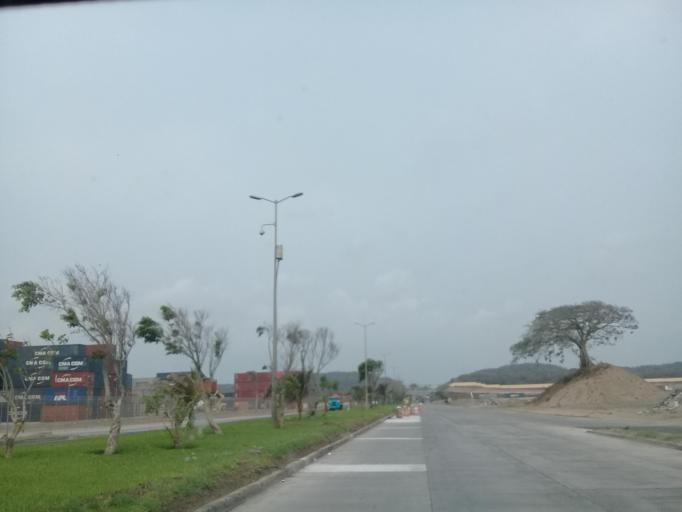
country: MX
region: Veracruz
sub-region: Veracruz
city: Rio Medio [Granja]
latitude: 19.2274
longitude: -96.1958
